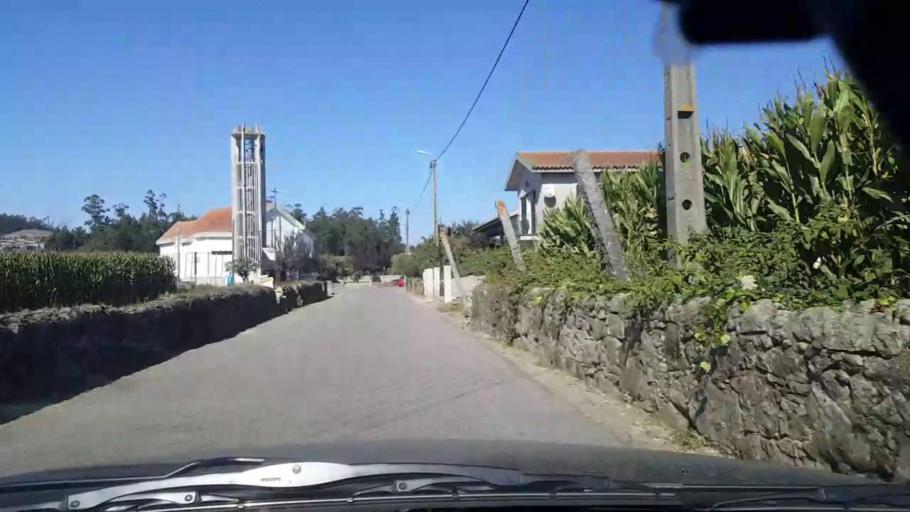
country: PT
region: Braga
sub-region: Vila Nova de Famalicao
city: Ribeirao
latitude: 41.3729
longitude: -8.6438
